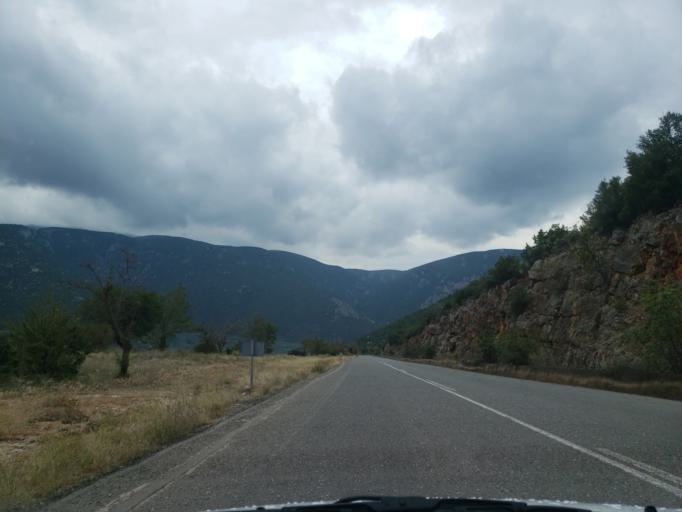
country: GR
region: Central Greece
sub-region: Nomos Fokidos
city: Amfissa
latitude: 38.5442
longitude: 22.4080
